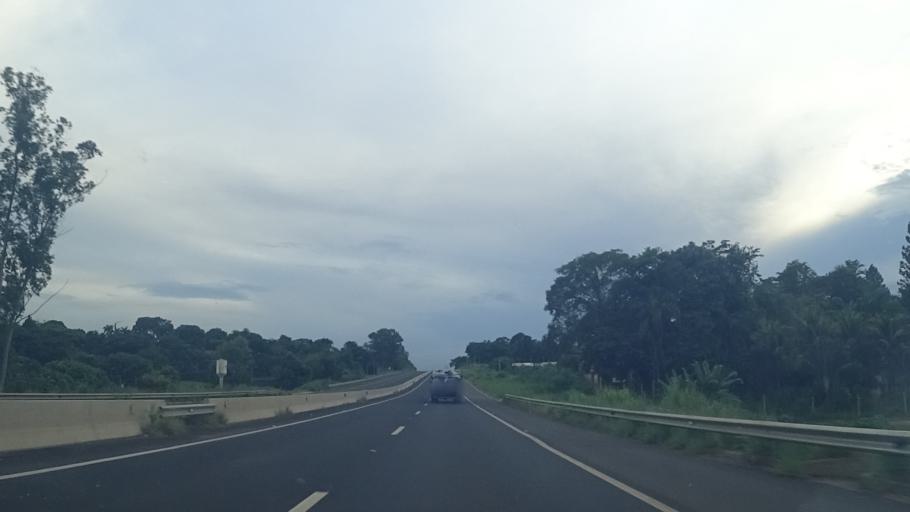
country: BR
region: Sao Paulo
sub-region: Regente Feijo
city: Regente Feijo
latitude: -22.1708
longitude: -51.3367
